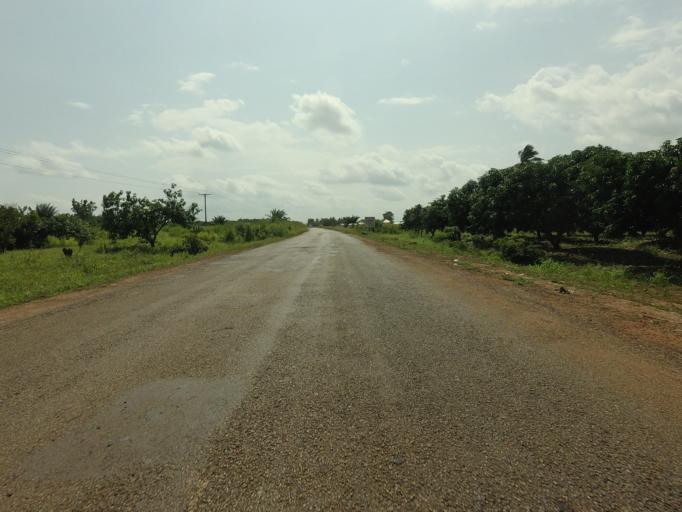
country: TG
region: Maritime
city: Lome
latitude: 6.2543
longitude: 0.9680
